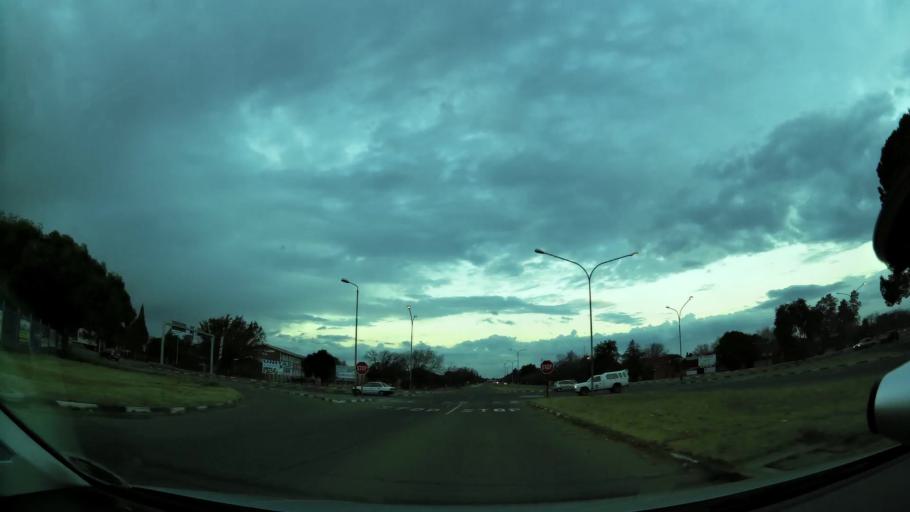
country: ZA
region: Orange Free State
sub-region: Lejweleputswa District Municipality
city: Welkom
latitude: -27.9744
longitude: 26.7456
